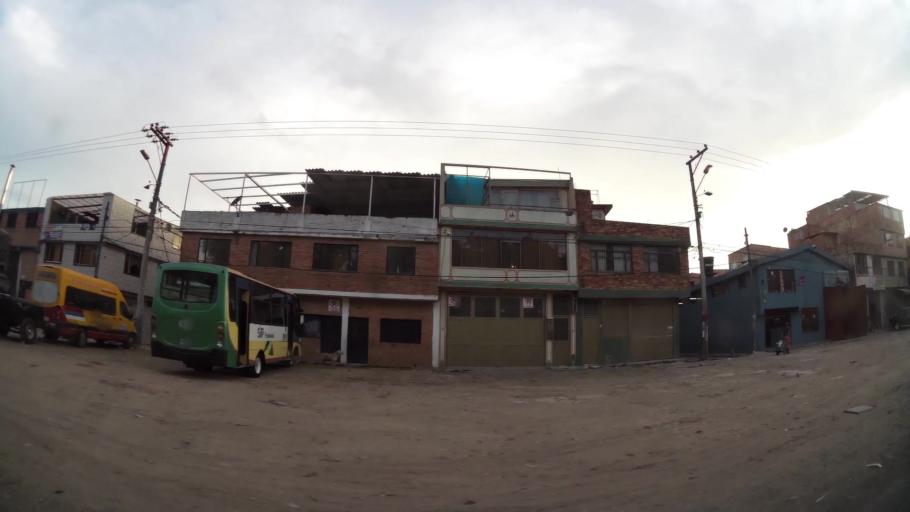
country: CO
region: Cundinamarca
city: Funza
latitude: 4.6928
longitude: -74.1487
